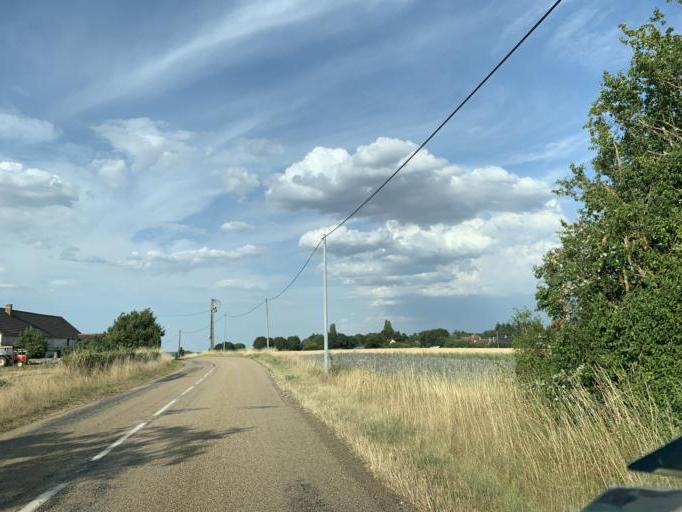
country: FR
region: Bourgogne
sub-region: Departement de l'Yonne
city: Fontenailles
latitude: 47.5213
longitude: 3.3796
